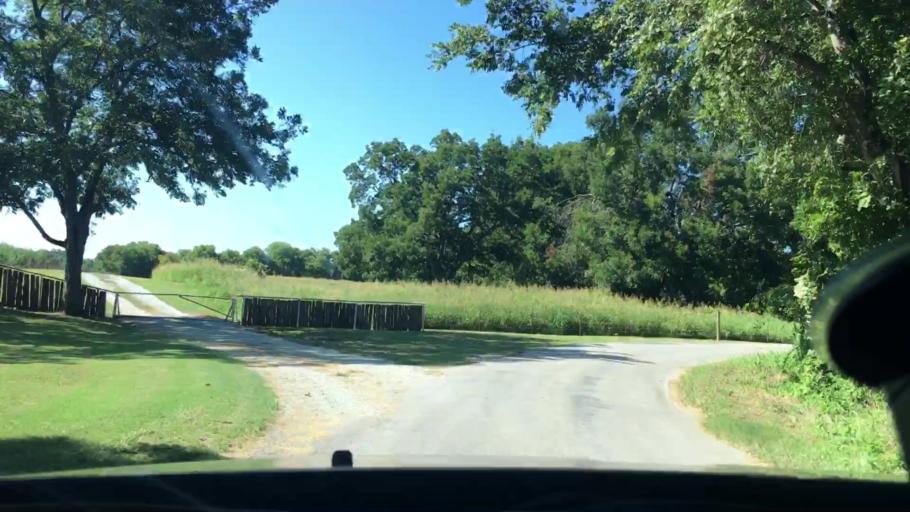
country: US
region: Oklahoma
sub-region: Pontotoc County
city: Ada
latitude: 34.7226
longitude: -96.6437
